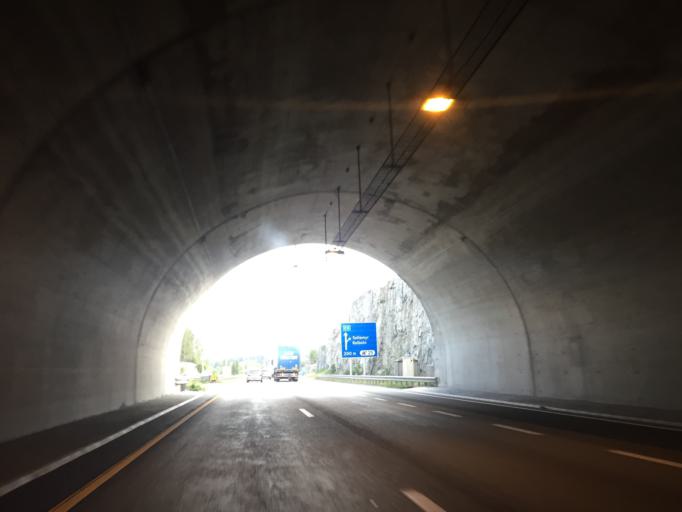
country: NO
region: Akershus
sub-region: Oppegard
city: Kolbotn
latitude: 59.7890
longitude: 10.8396
